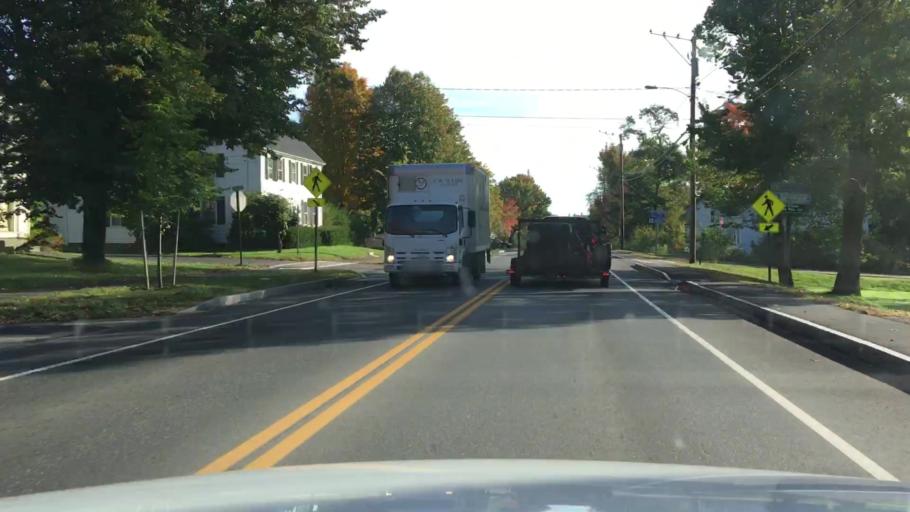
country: US
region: Maine
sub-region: Knox County
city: Thomaston
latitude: 44.0801
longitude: -69.1759
